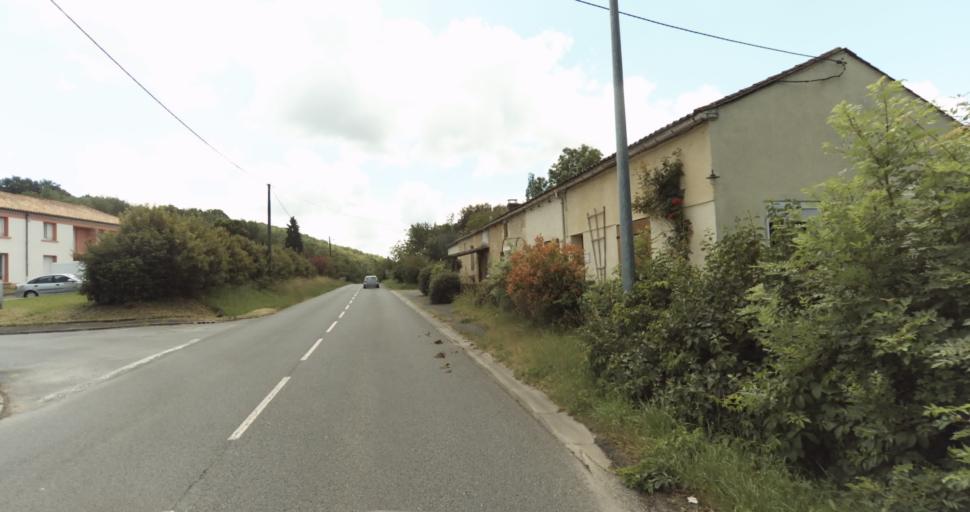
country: FR
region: Aquitaine
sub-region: Departement de la Dordogne
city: Lalinde
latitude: 44.8201
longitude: 0.7073
